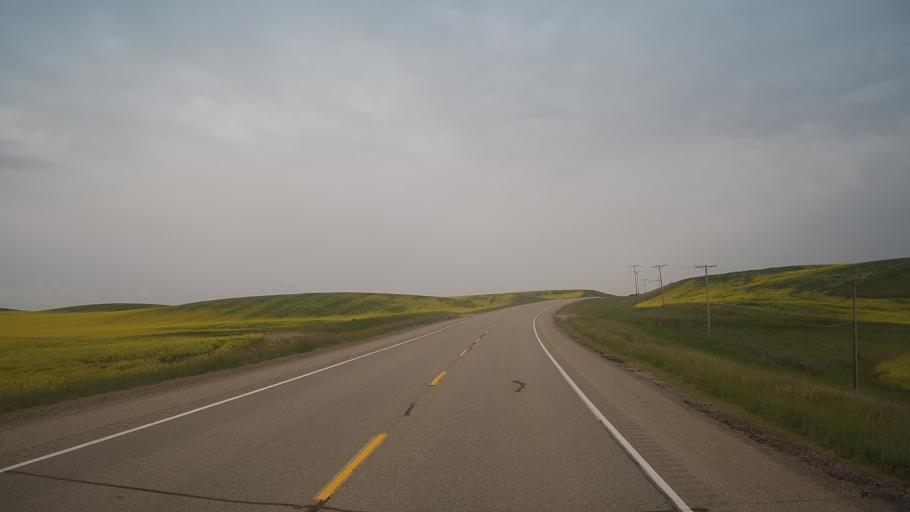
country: CA
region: Saskatchewan
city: Biggar
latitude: 52.0546
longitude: -107.7630
